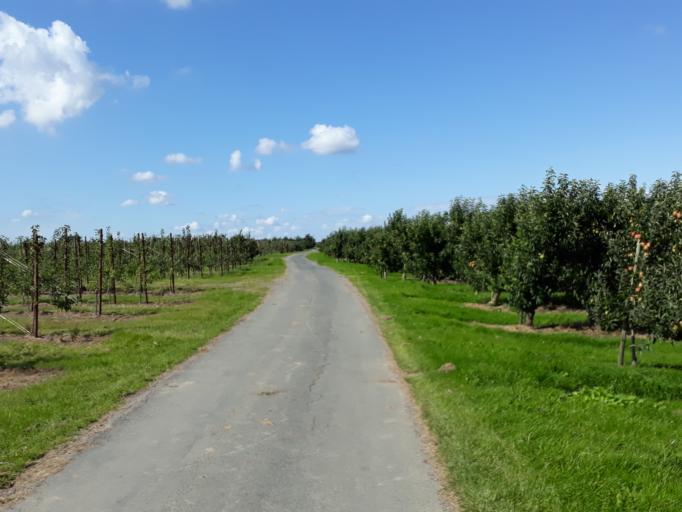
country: DE
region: Lower Saxony
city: Mittelnkirchen
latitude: 53.5445
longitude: 9.6330
